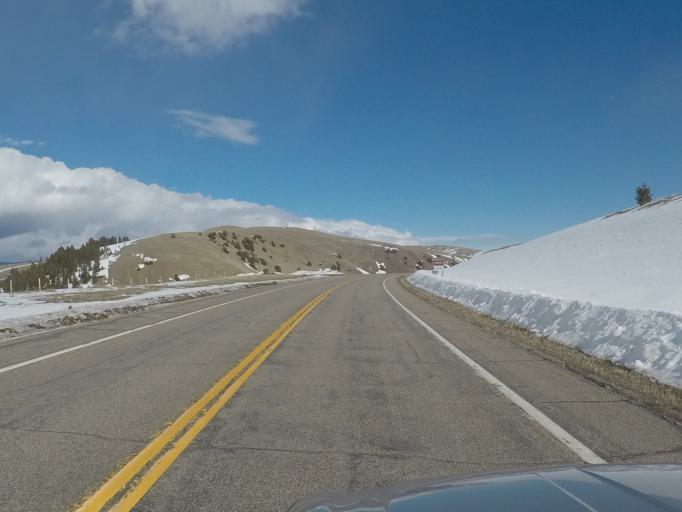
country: US
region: Montana
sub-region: Meagher County
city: White Sulphur Springs
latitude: 46.6223
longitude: -110.7054
